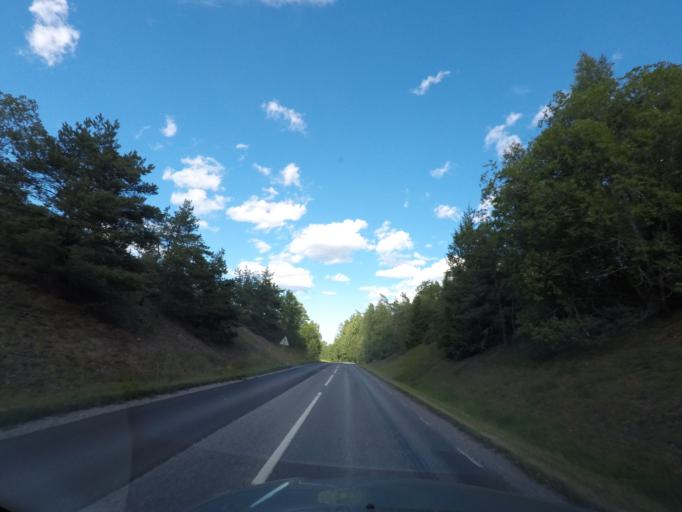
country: SE
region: Stockholm
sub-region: Sigtuna Kommun
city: Marsta
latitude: 59.6999
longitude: 17.9681
